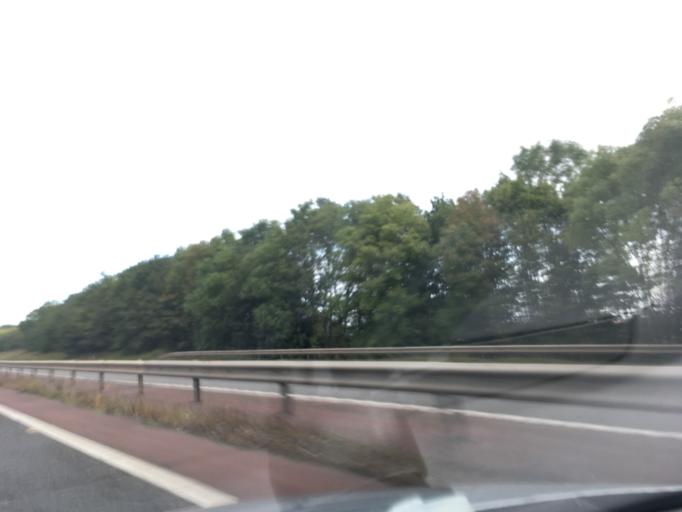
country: GB
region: England
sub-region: Oxfordshire
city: Adderbury
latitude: 52.0273
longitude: -1.2978
